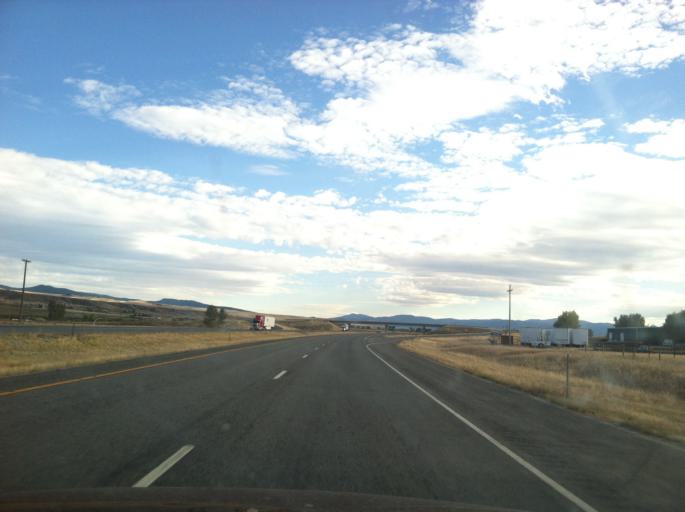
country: US
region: Montana
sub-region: Deer Lodge County
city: Warm Springs
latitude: 46.2746
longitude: -112.7475
